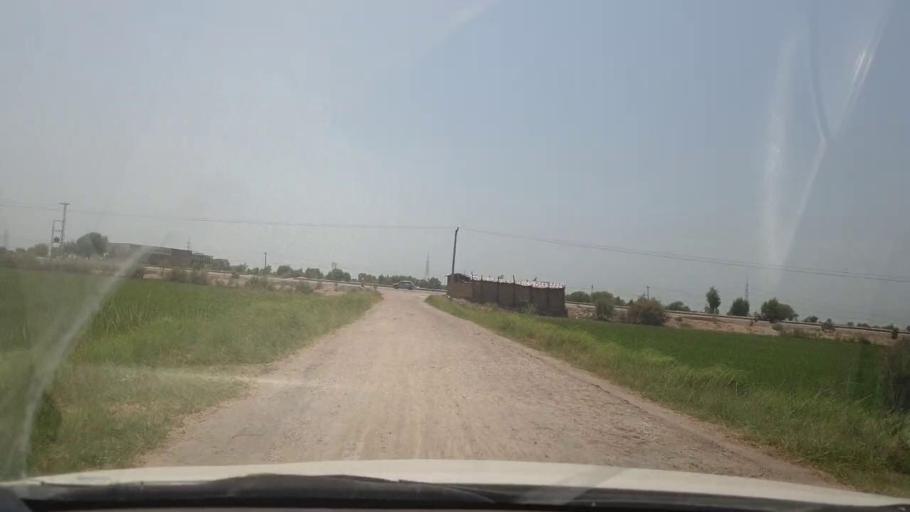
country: PK
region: Sindh
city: Lakhi
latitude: 27.8719
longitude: 68.6893
